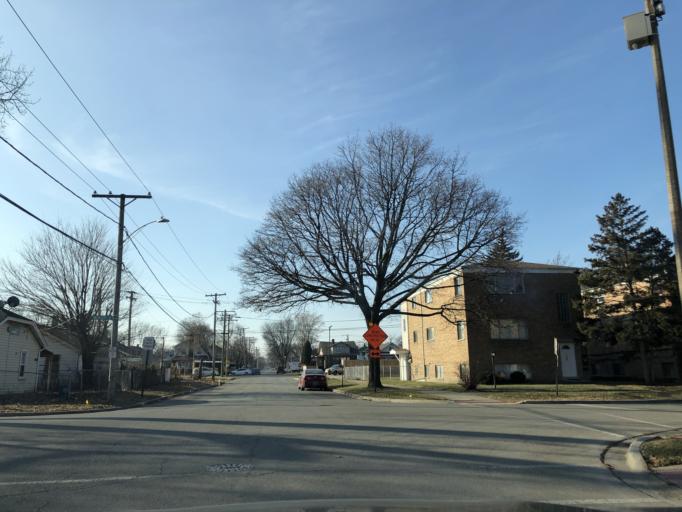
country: US
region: Illinois
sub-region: Cook County
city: Maywood
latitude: 41.8773
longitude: -87.8326
